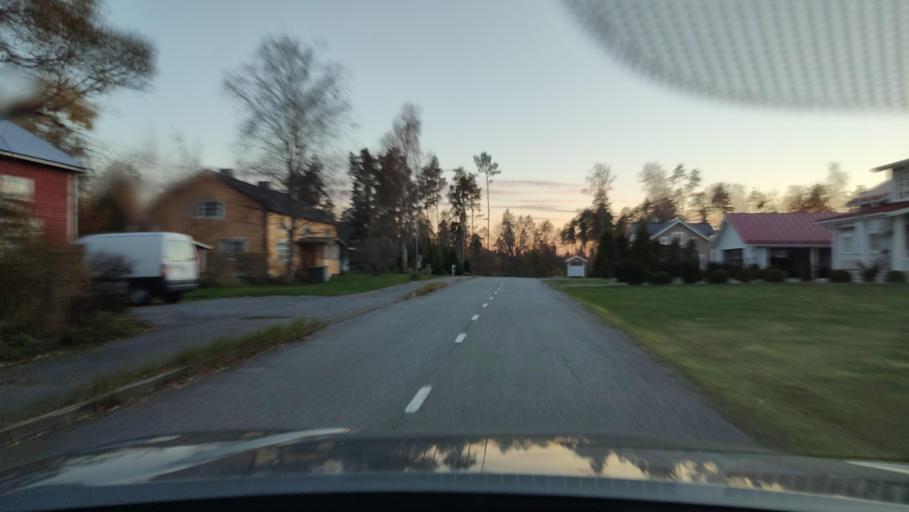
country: FI
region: Ostrobothnia
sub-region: Sydosterbotten
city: Kristinestad
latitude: 62.2675
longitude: 21.3894
